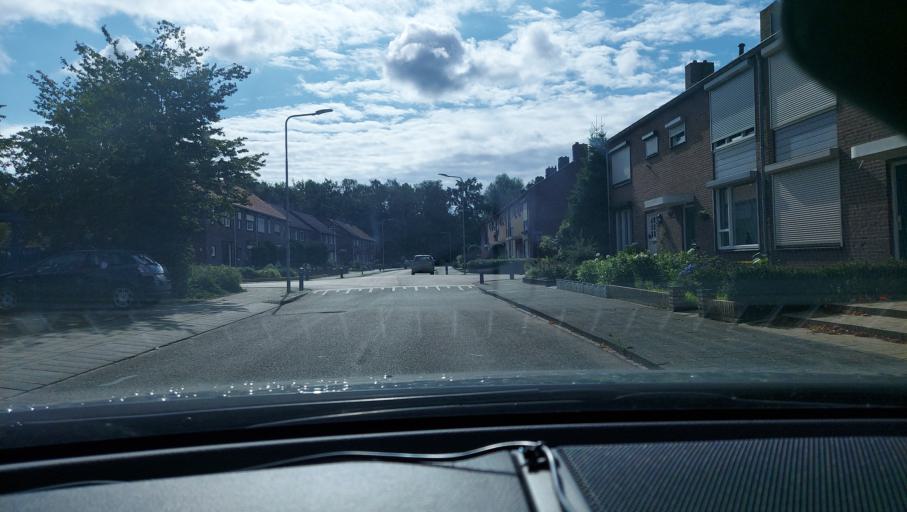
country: NL
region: Limburg
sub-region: Gemeente Beesel
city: Offenbeek
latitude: 51.2856
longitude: 6.0942
